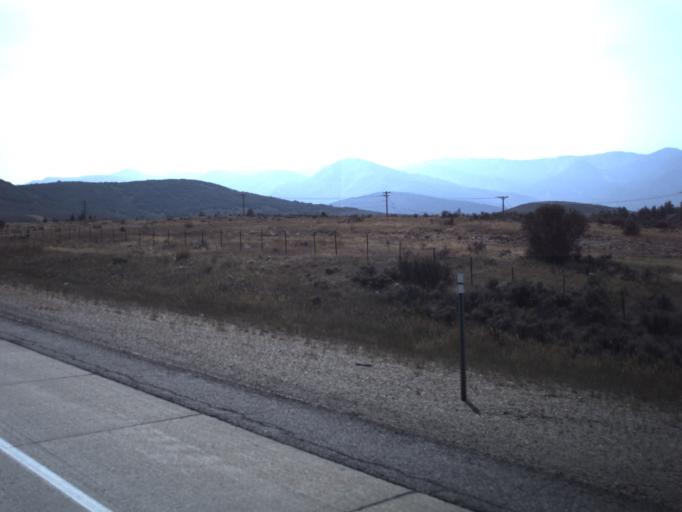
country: US
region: Utah
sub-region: Summit County
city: Snyderville
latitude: 40.7186
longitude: -111.4887
